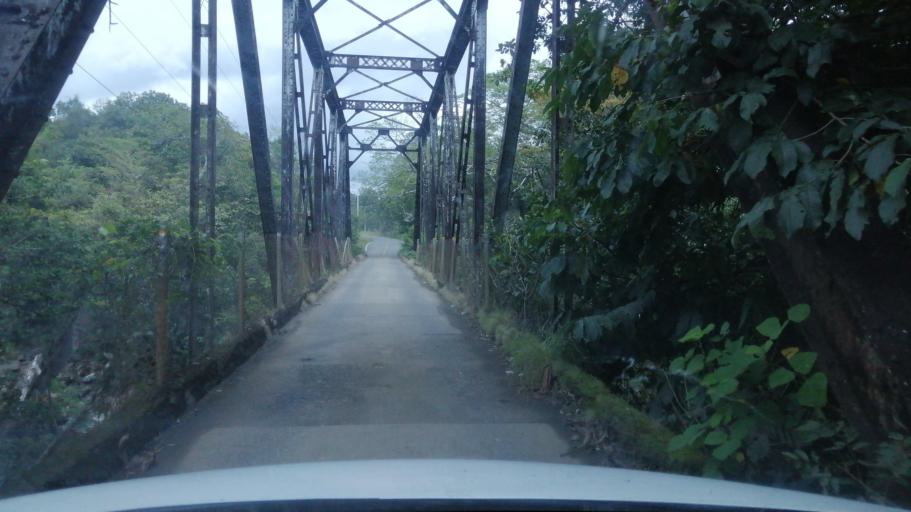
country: PA
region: Chiriqui
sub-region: Distrito Dolega
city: Pueblo Nuevo
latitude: 8.5950
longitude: -82.4137
